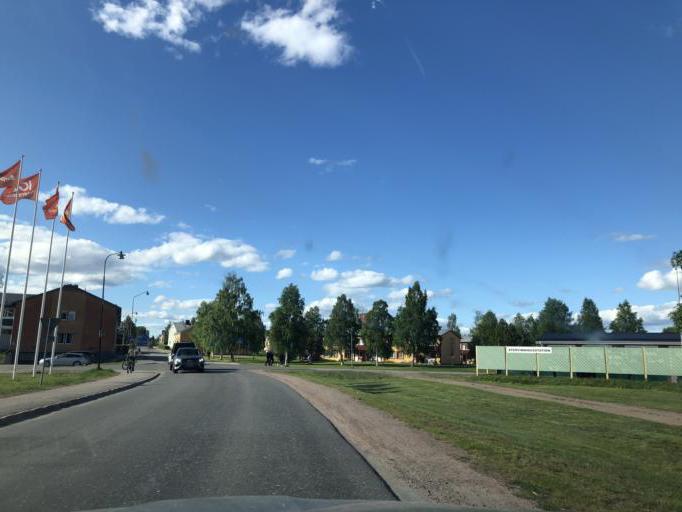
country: SE
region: Norrbotten
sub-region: Overkalix Kommun
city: OEverkalix
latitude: 66.3229
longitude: 22.8482
